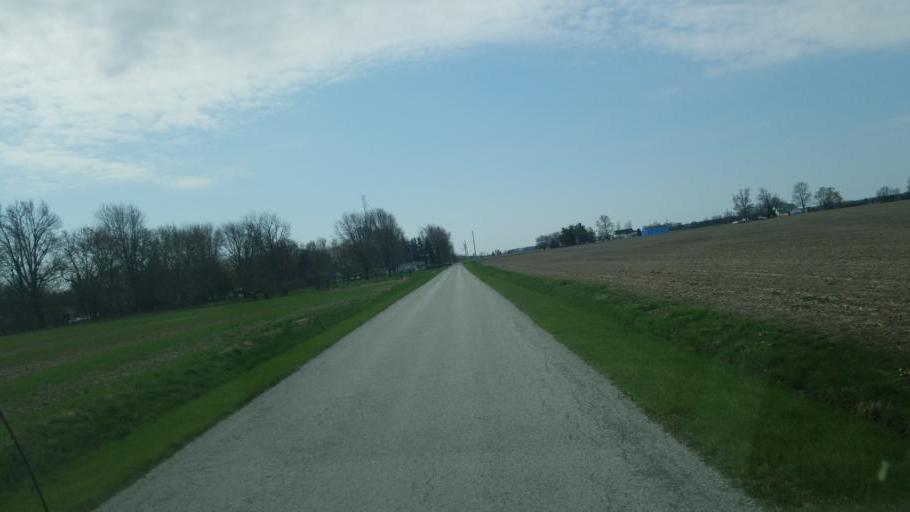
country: US
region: Ohio
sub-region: Delaware County
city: Ashley
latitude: 40.4136
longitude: -82.9635
